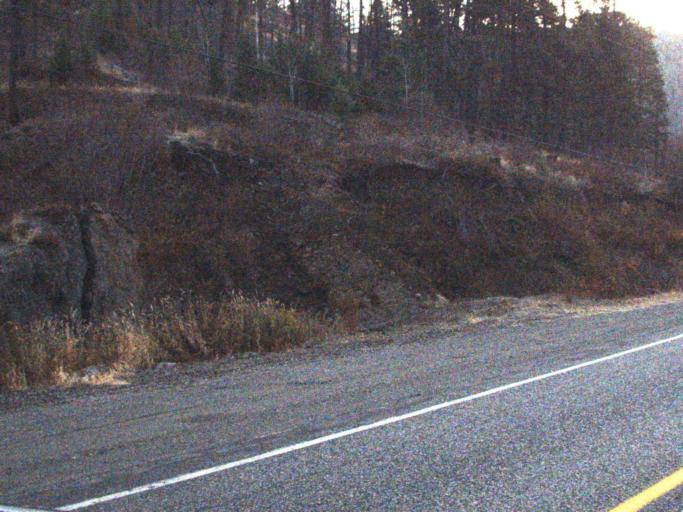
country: US
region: Washington
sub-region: Ferry County
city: Republic
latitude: 48.5414
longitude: -118.7451
